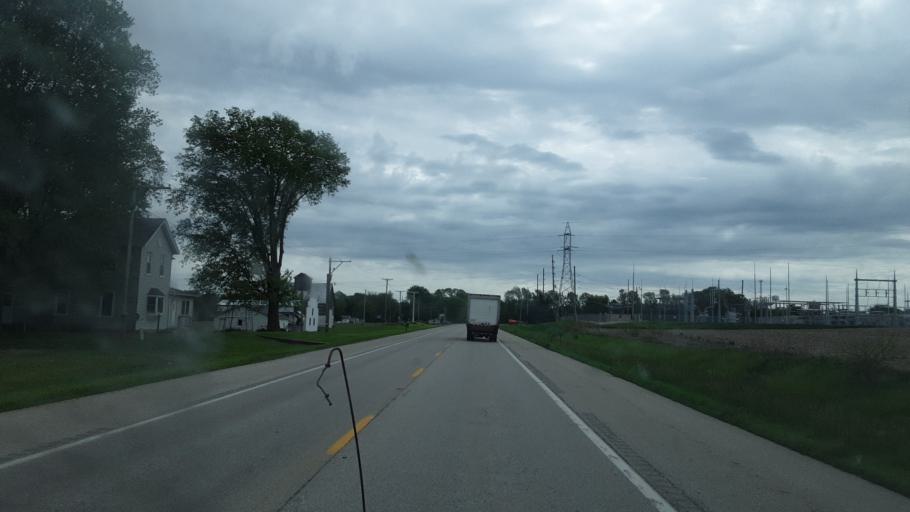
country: US
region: Illinois
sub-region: Tazewell County
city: Delavan
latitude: 40.3054
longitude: -89.6143
